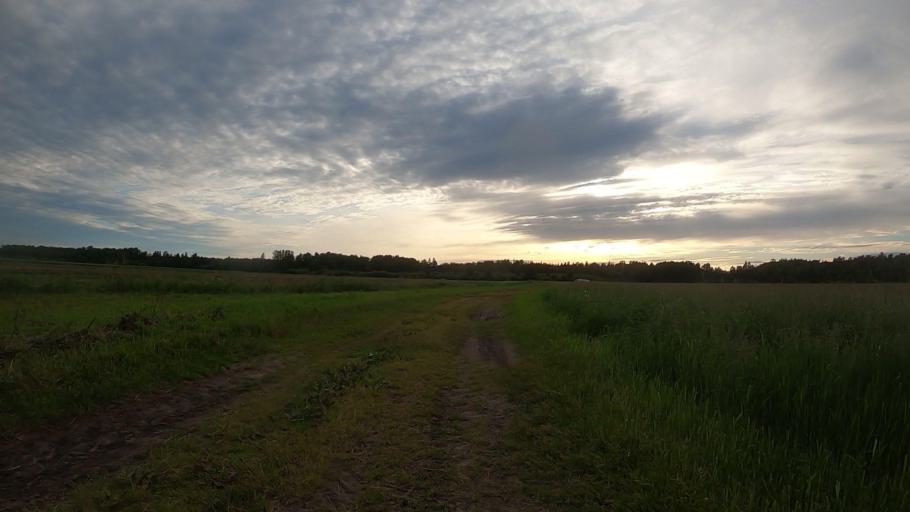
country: LV
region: Olaine
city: Olaine
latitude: 56.8247
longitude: 23.9480
